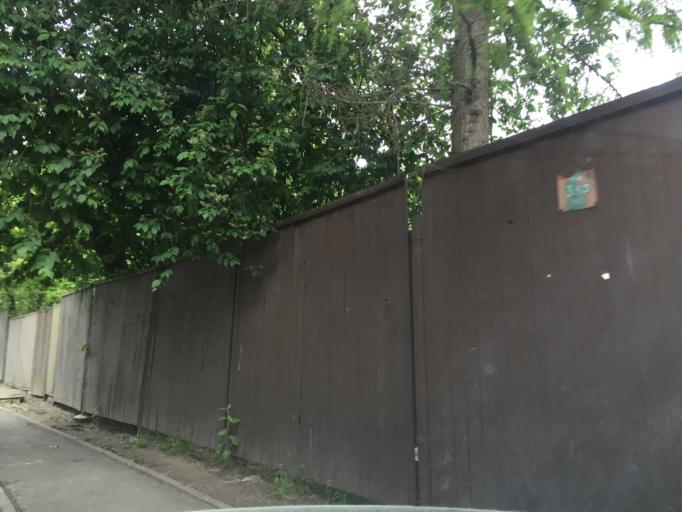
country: LV
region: Riga
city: Riga
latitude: 56.9758
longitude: 24.1417
